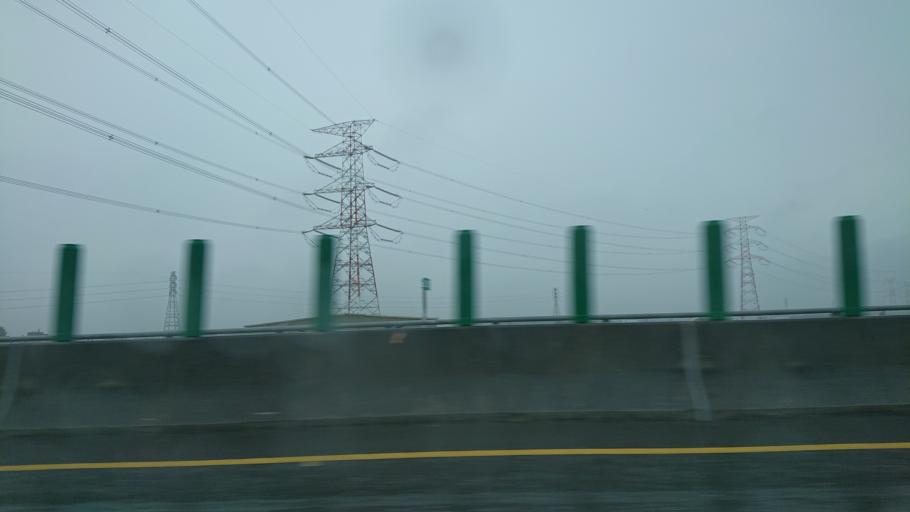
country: TW
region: Taiwan
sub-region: Yunlin
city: Douliu
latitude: 23.7770
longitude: 120.2734
